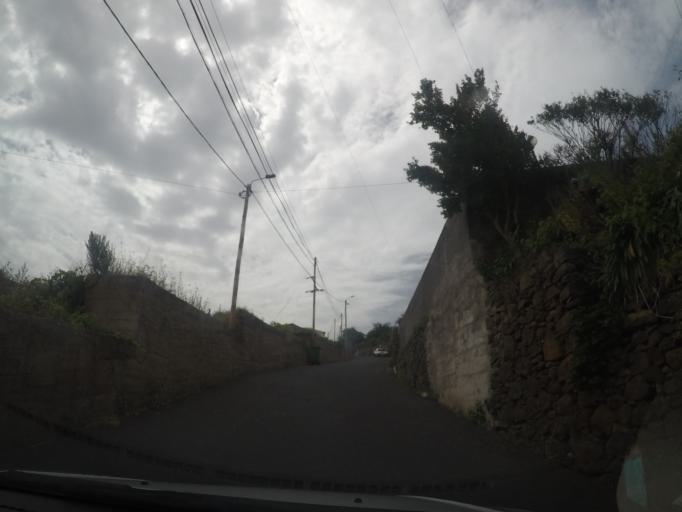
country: PT
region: Madeira
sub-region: Santa Cruz
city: Santa Cruz
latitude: 32.6880
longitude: -16.8091
